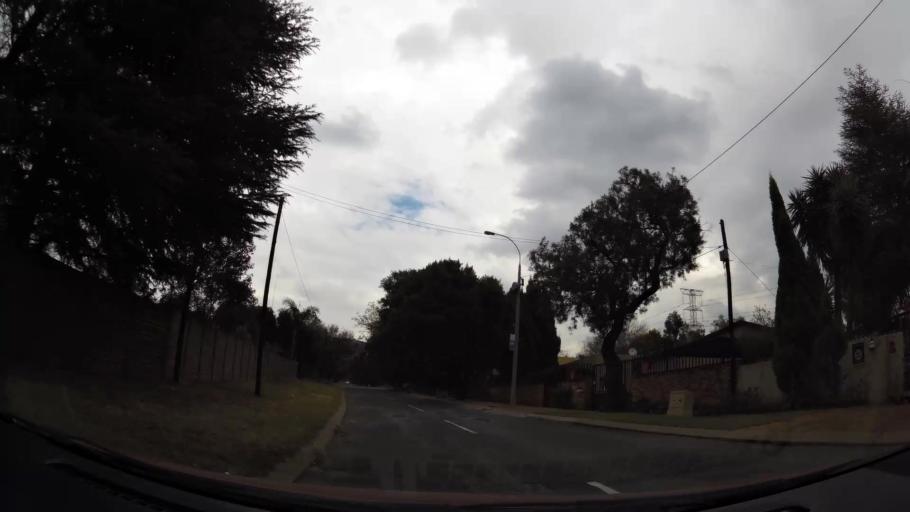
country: ZA
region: Gauteng
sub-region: City of Johannesburg Metropolitan Municipality
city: Roodepoort
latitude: -26.1153
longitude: 27.9010
